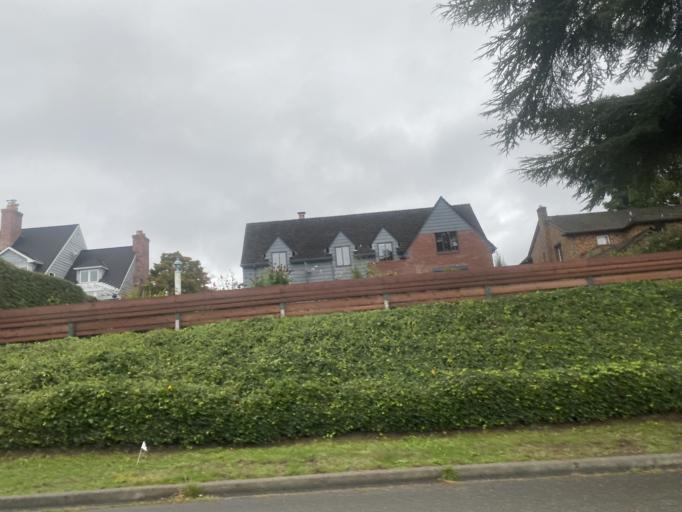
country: US
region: Washington
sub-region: King County
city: Seattle
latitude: 47.6369
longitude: -122.4067
